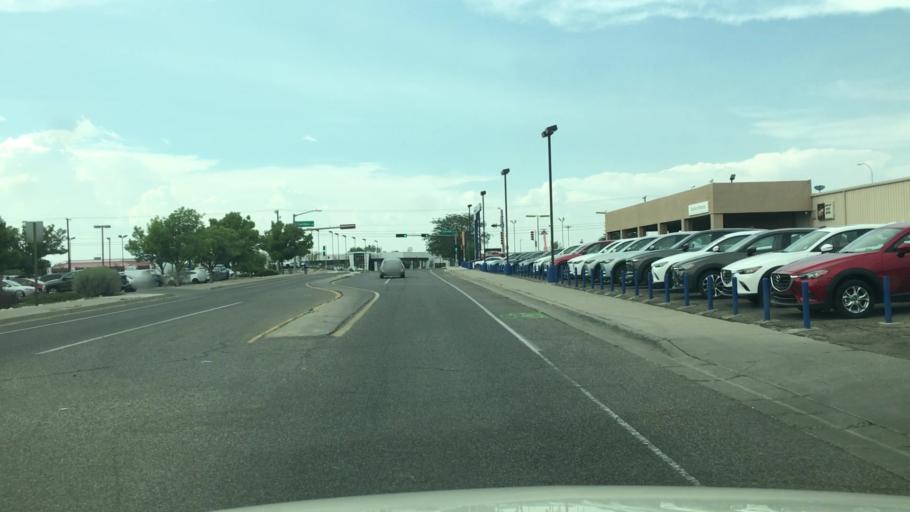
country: US
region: New Mexico
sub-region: Santa Fe County
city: Agua Fria
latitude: 35.6570
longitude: -105.9854
